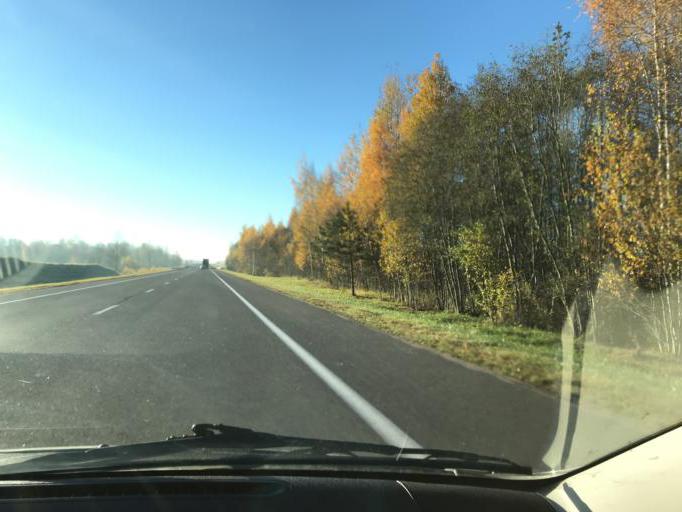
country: BY
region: Vitebsk
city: Vitebsk
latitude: 55.0058
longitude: 30.3340
